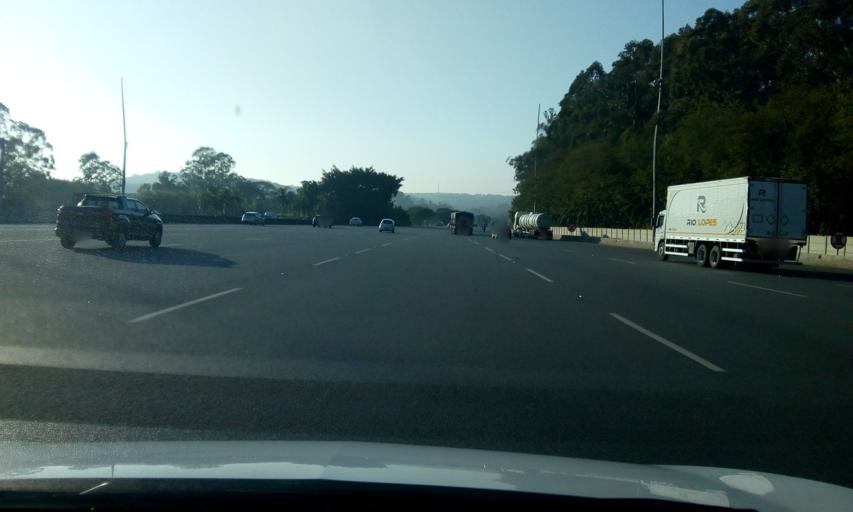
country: BR
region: Sao Paulo
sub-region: Vinhedo
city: Vinhedo
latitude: -23.0591
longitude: -47.0436
